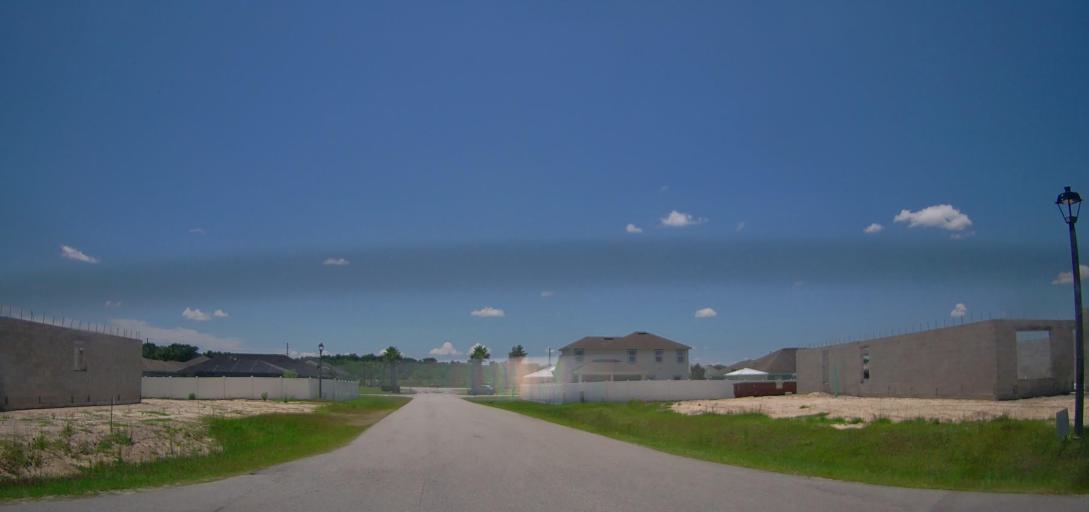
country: US
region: Florida
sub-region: Marion County
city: Belleview
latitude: 29.0880
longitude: -82.0634
